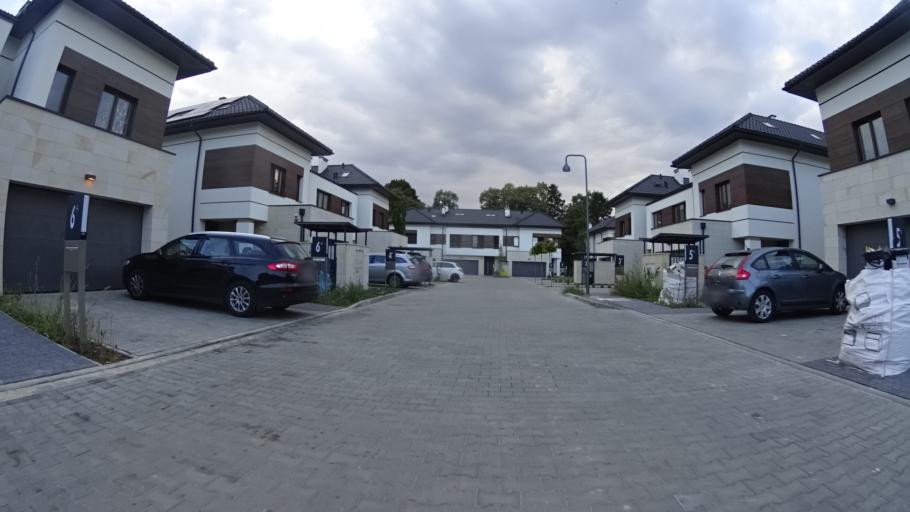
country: PL
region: Masovian Voivodeship
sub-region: Powiat warszawski zachodni
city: Ozarow Mazowiecki
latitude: 52.2325
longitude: 20.8067
